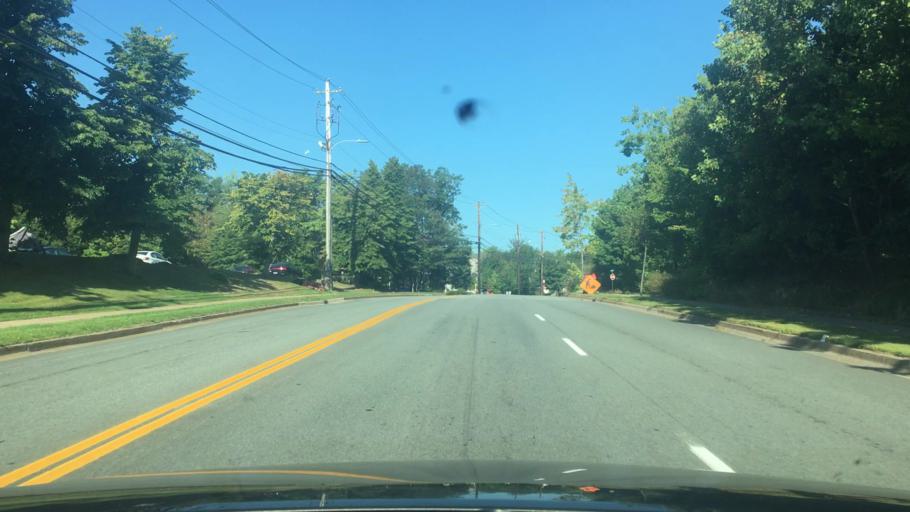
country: CA
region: Nova Scotia
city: Dartmouth
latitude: 44.7156
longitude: -63.6800
